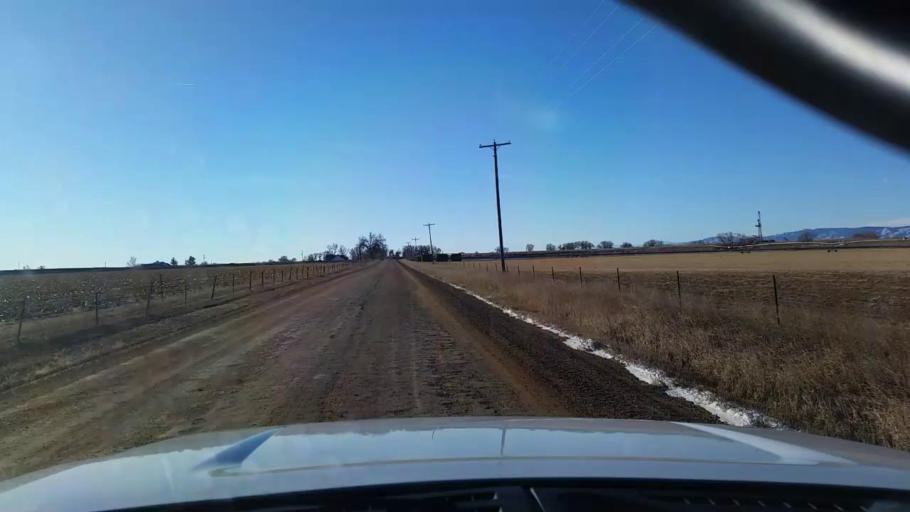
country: US
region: Colorado
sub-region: Larimer County
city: Wellington
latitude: 40.7692
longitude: -105.0382
